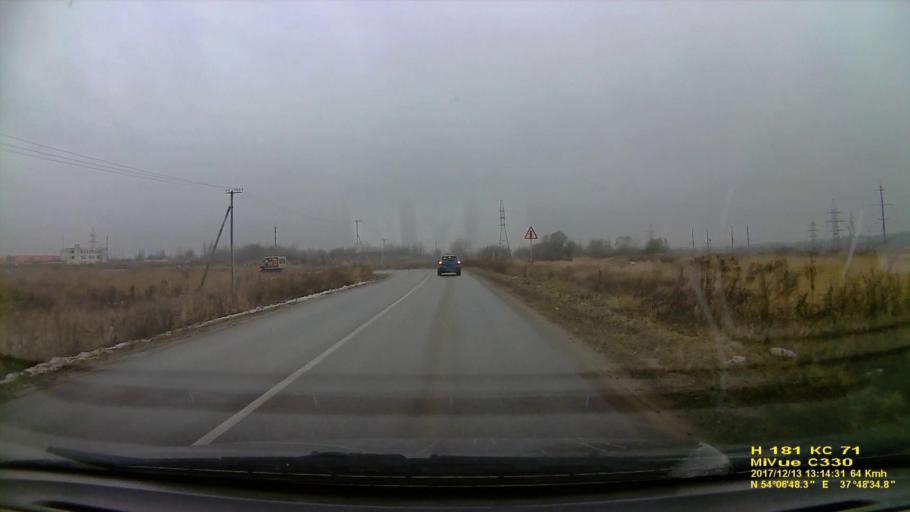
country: RU
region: Tula
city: Bolokhovo
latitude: 54.1129
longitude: 37.8103
